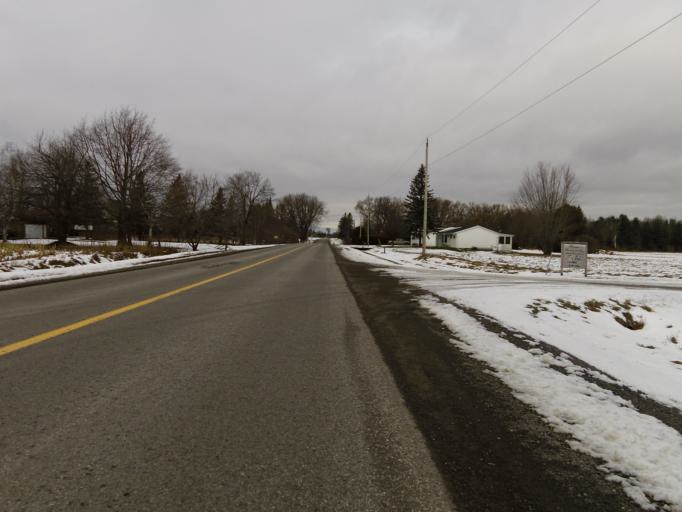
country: CA
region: Ontario
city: Carleton Place
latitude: 45.3460
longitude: -76.0835
